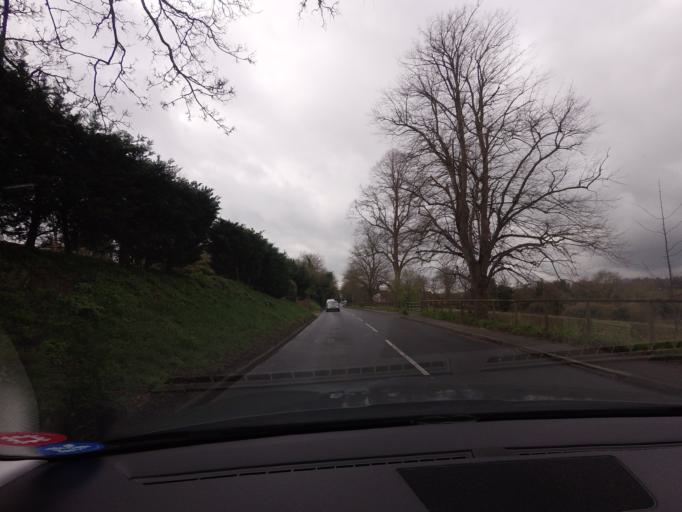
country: GB
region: England
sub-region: Kent
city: Eynsford
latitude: 51.3741
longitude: 0.2201
